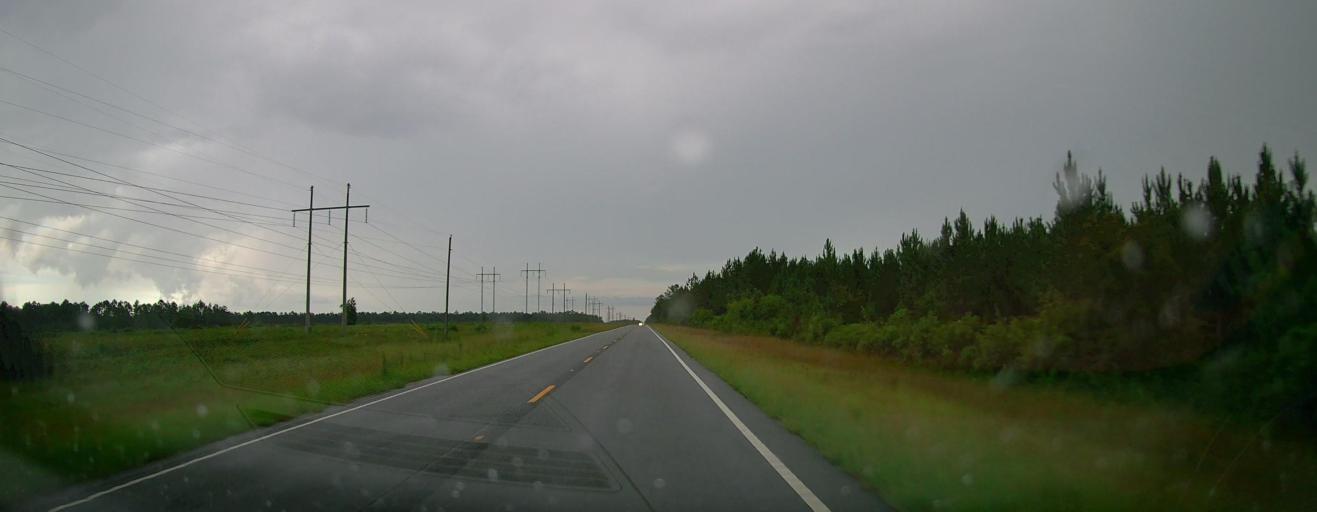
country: US
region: Georgia
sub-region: Brantley County
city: Nahunta
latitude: 31.3375
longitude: -81.8656
